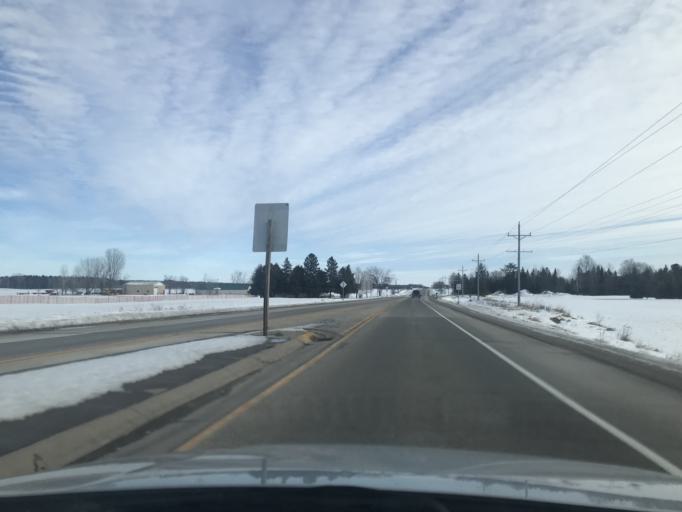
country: US
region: Wisconsin
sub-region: Oconto County
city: Gillett
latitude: 44.8961
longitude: -88.2448
